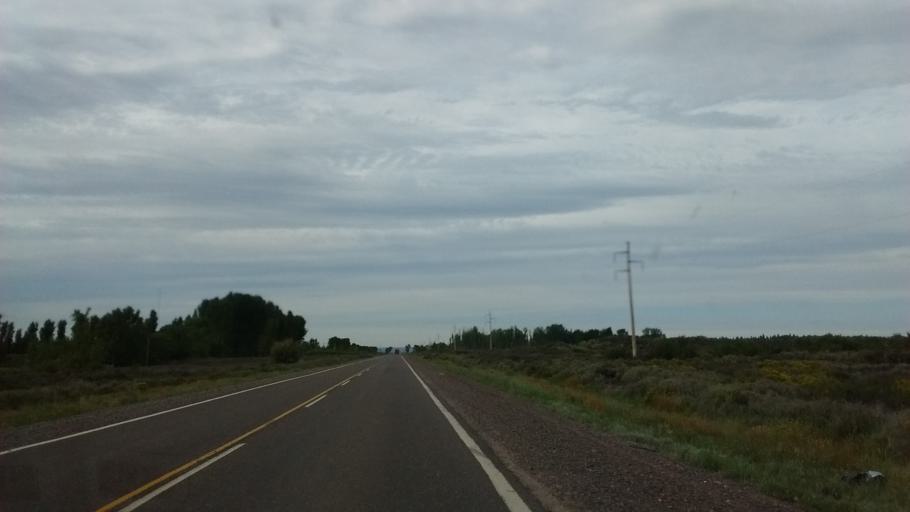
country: AR
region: Rio Negro
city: Catriel
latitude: -37.9050
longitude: -67.8644
